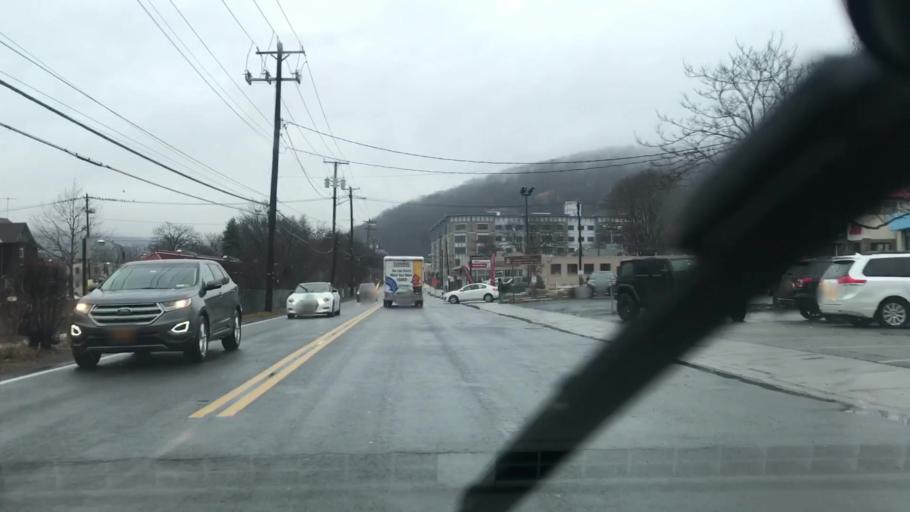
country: US
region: New York
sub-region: Rockland County
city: Suffern
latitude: 41.1129
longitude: -74.1529
